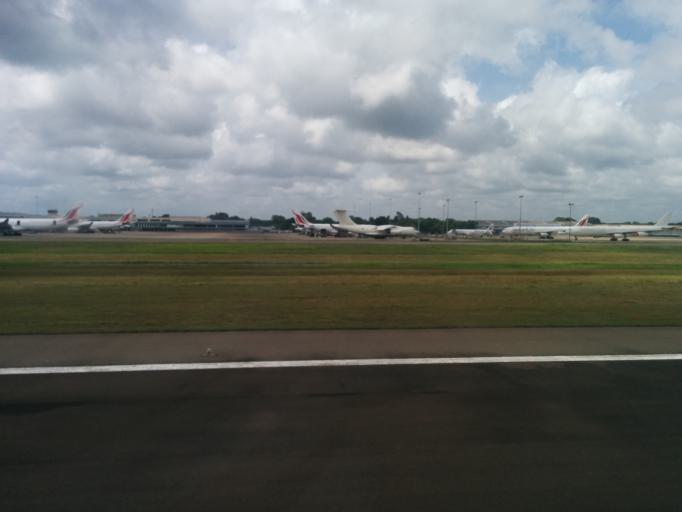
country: LK
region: Western
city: Katunayaka
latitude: 7.1772
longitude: 79.8808
